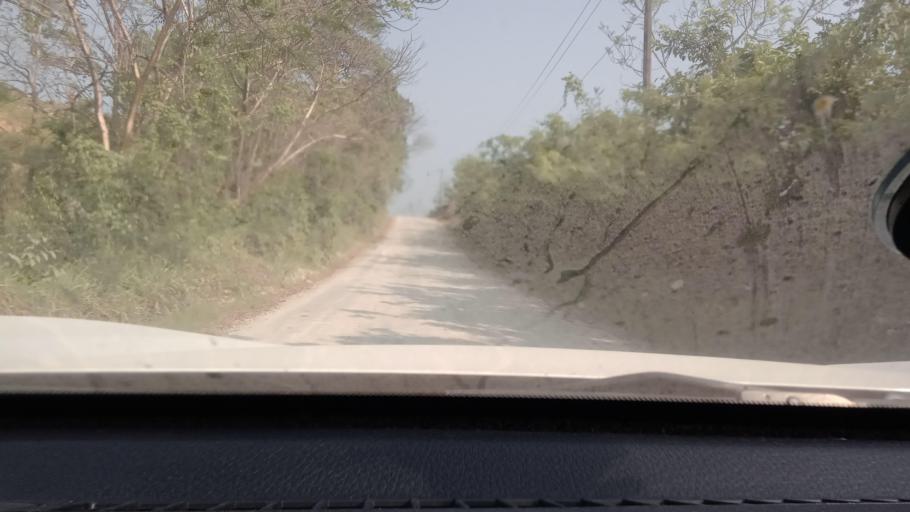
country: MX
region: Tabasco
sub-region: Huimanguillo
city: Francisco Rueda
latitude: 17.6137
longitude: -93.9384
